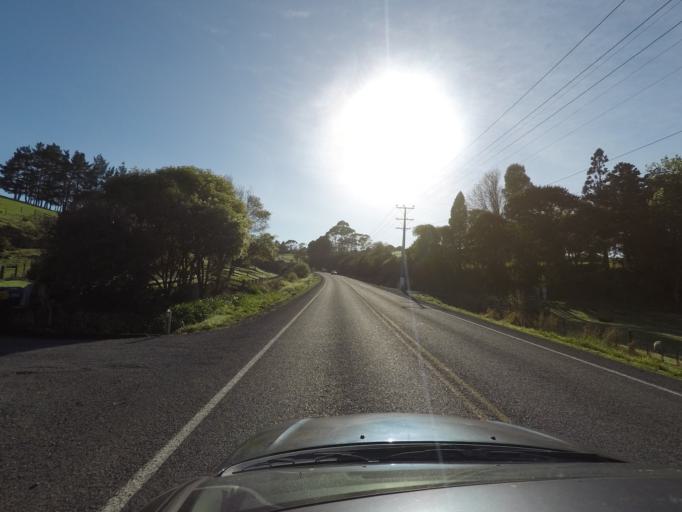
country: NZ
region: Auckland
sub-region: Auckland
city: Red Hill
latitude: -36.9962
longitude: 174.9813
